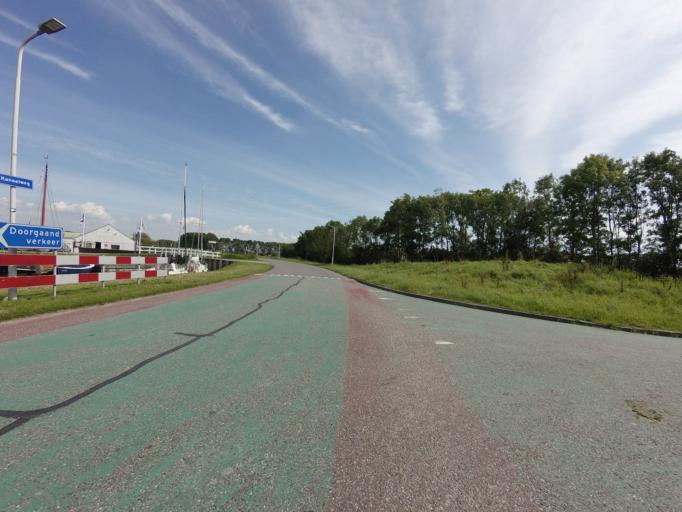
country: NL
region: Friesland
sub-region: Gemeente Harlingen
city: Harlingen
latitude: 53.1732
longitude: 5.4538
